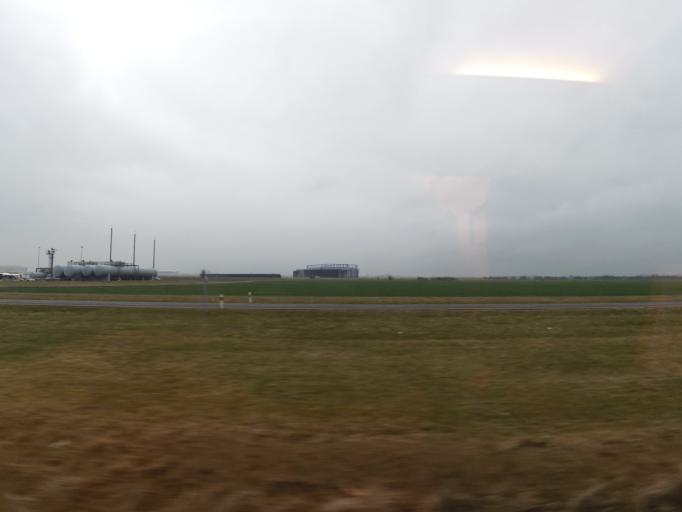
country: DE
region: Saxony
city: Schkeuditz
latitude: 51.4249
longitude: 12.2067
